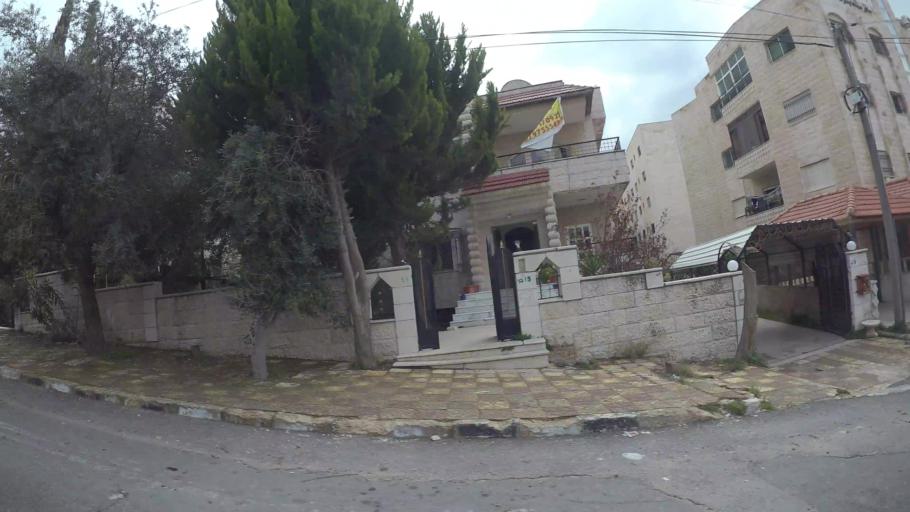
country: JO
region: Amman
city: Umm as Summaq
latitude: 31.8969
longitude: 35.8628
